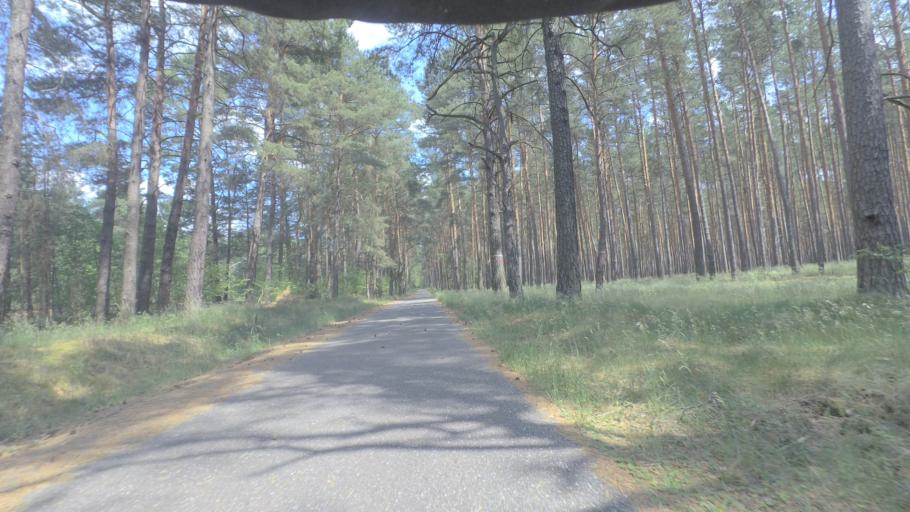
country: DE
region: Brandenburg
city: Fichtenwalde
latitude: 52.2418
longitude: 12.8815
